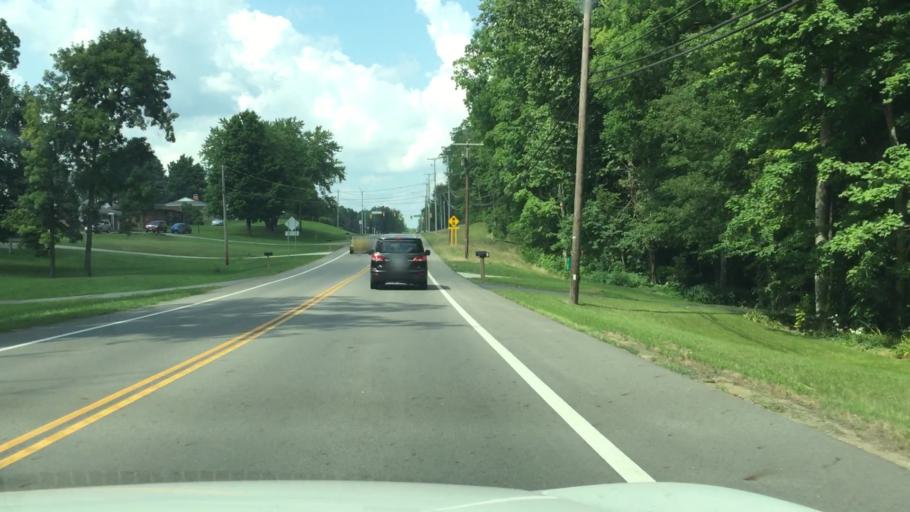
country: US
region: Ohio
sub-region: Clark County
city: Northridge
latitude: 39.9823
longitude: -83.7834
